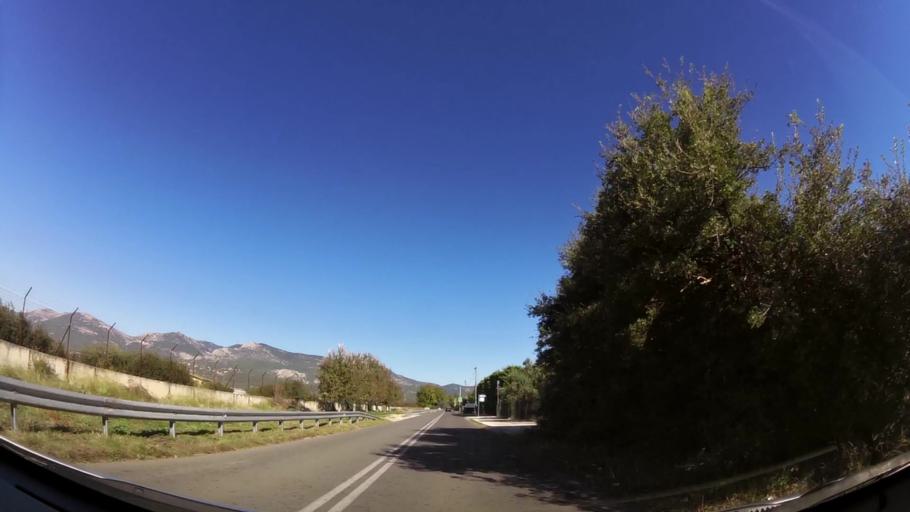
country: GR
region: Attica
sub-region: Nomarchia Anatolikis Attikis
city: Varybobi
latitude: 38.1116
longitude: 23.7904
